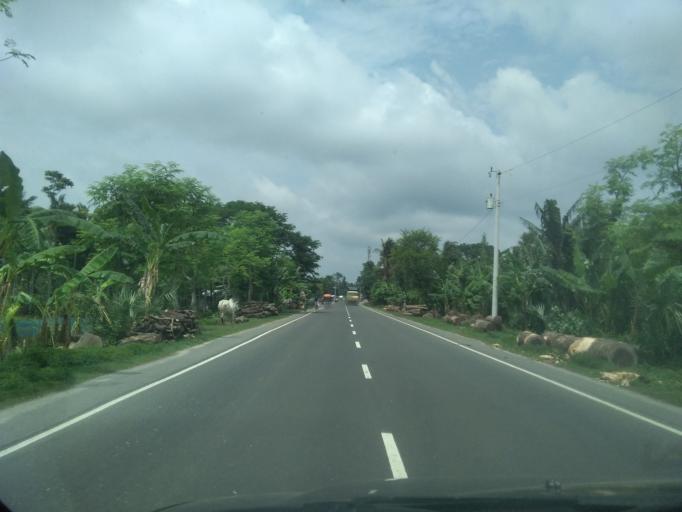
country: BD
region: Khulna
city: Kesabpur
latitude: 22.7813
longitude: 89.2064
